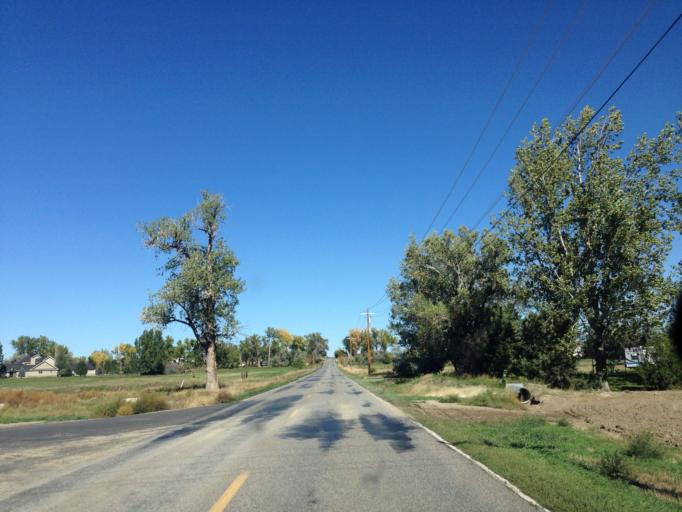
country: US
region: Montana
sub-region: Yellowstone County
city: Laurel
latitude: 45.7579
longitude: -108.6795
